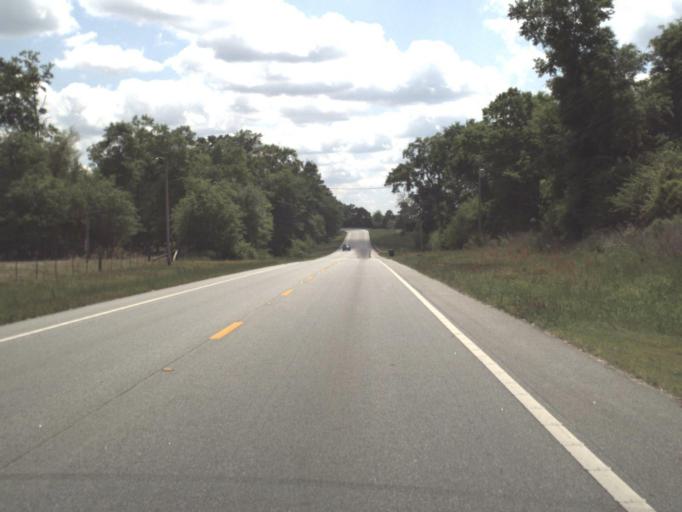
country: US
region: Alabama
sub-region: Escambia County
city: Atmore
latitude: 30.9887
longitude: -87.4909
